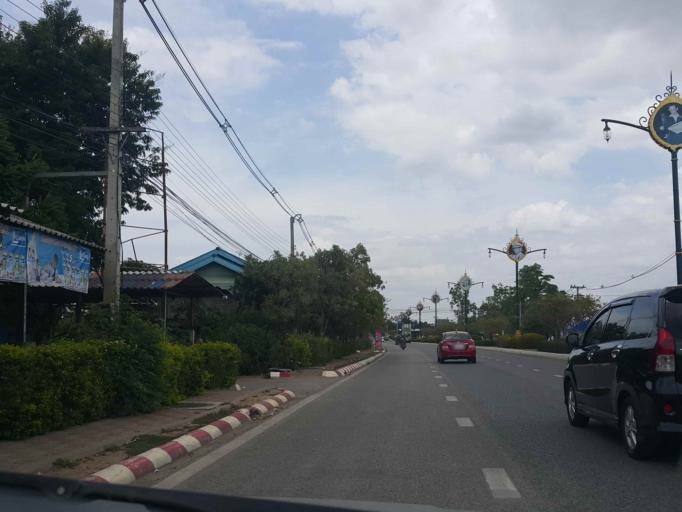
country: TH
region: Chiang Mai
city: Hang Dong
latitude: 18.7417
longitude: 98.9308
